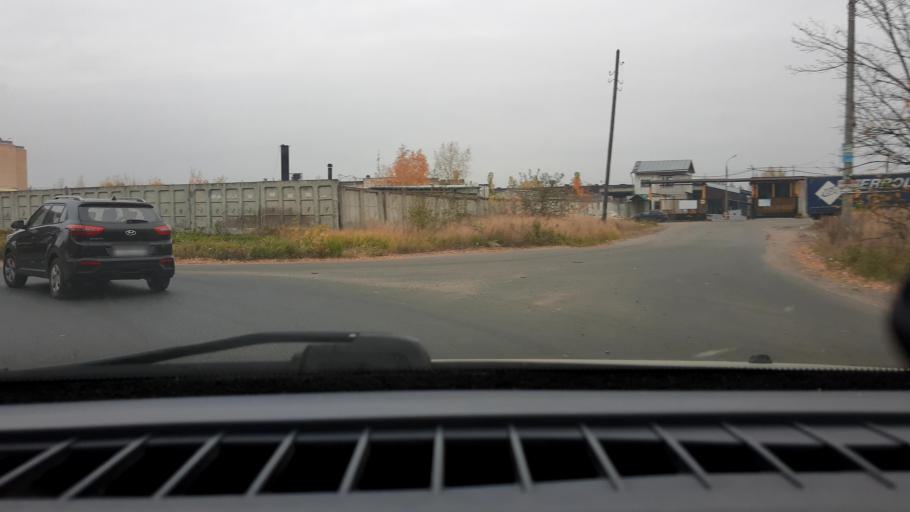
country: RU
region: Nizjnij Novgorod
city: Gorbatovka
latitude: 56.3319
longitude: 43.8140
